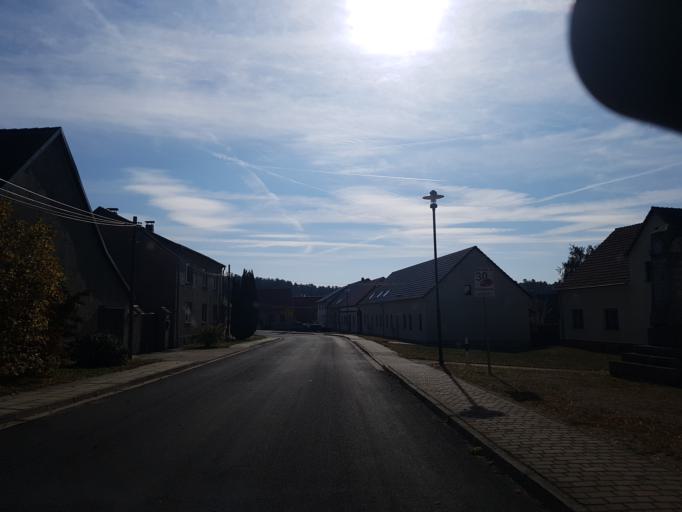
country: DE
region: Brandenburg
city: Hohenbucko
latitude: 51.7063
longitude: 13.4904
